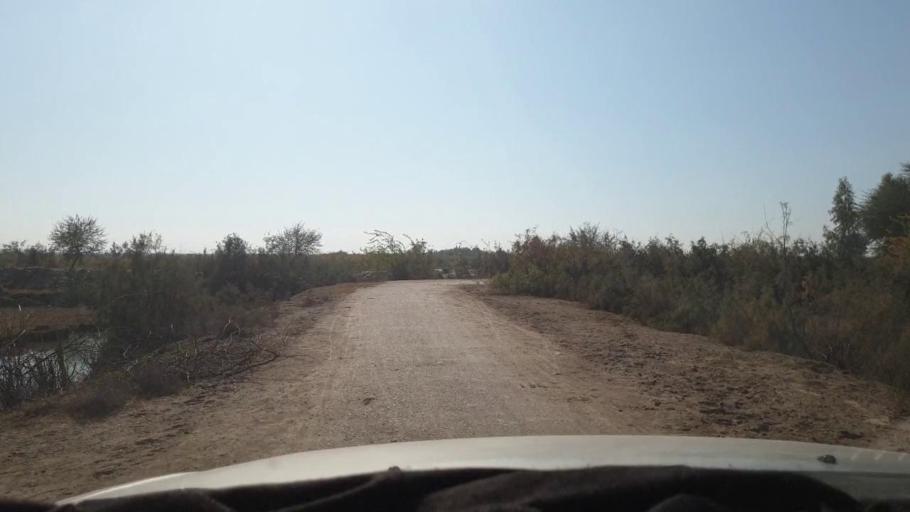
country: PK
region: Sindh
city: Adilpur
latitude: 27.8951
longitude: 69.2511
